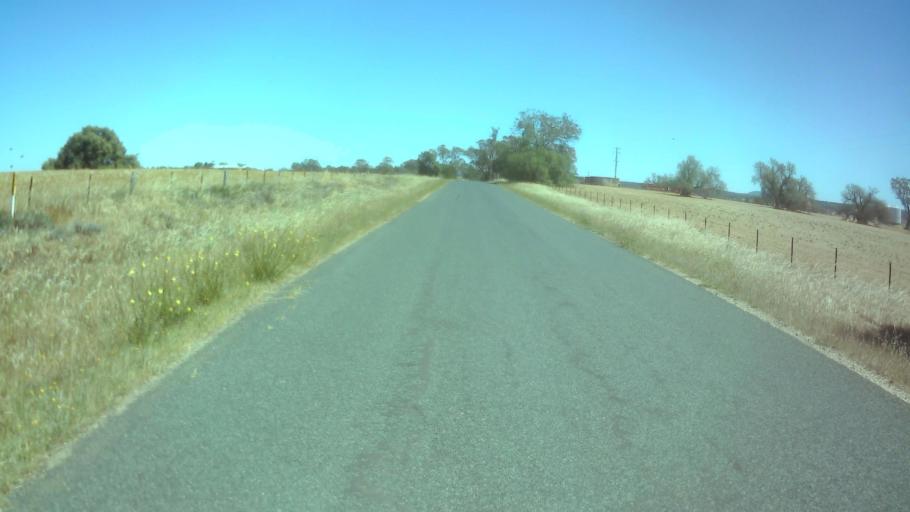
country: AU
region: New South Wales
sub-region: Weddin
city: Grenfell
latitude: -33.9516
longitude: 148.3975
